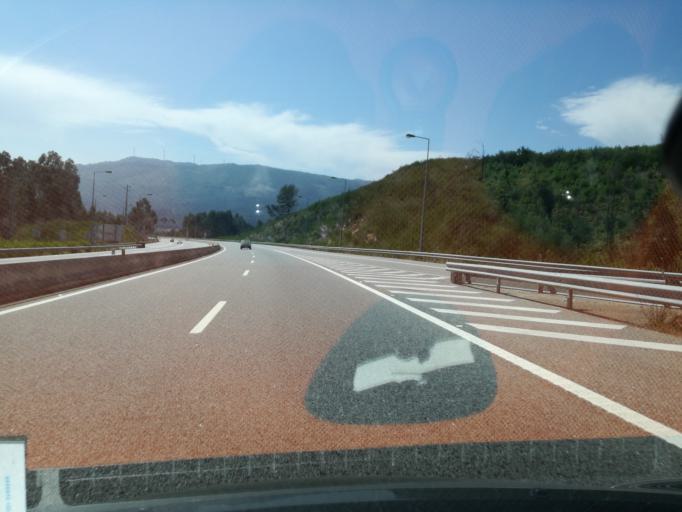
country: PT
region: Viana do Castelo
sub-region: Caminha
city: Vila Praia de Ancora
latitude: 41.8147
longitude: -8.8051
